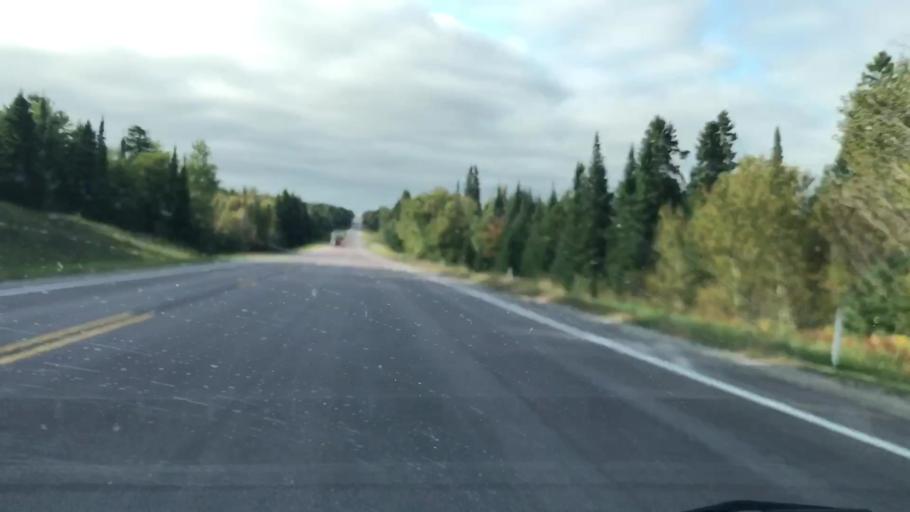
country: US
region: Michigan
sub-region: Luce County
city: Newberry
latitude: 46.3024
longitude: -85.5682
